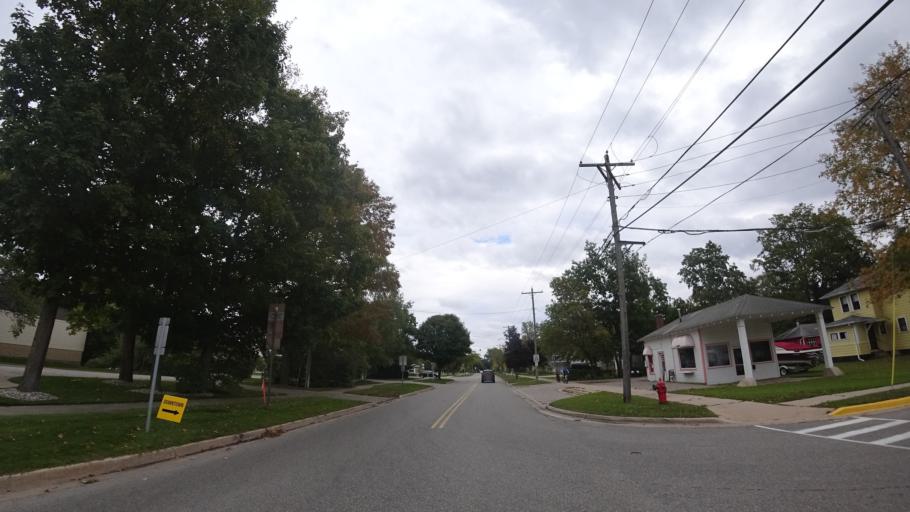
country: US
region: Michigan
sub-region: Emmet County
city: Harbor Springs
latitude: 45.4353
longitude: -84.9917
